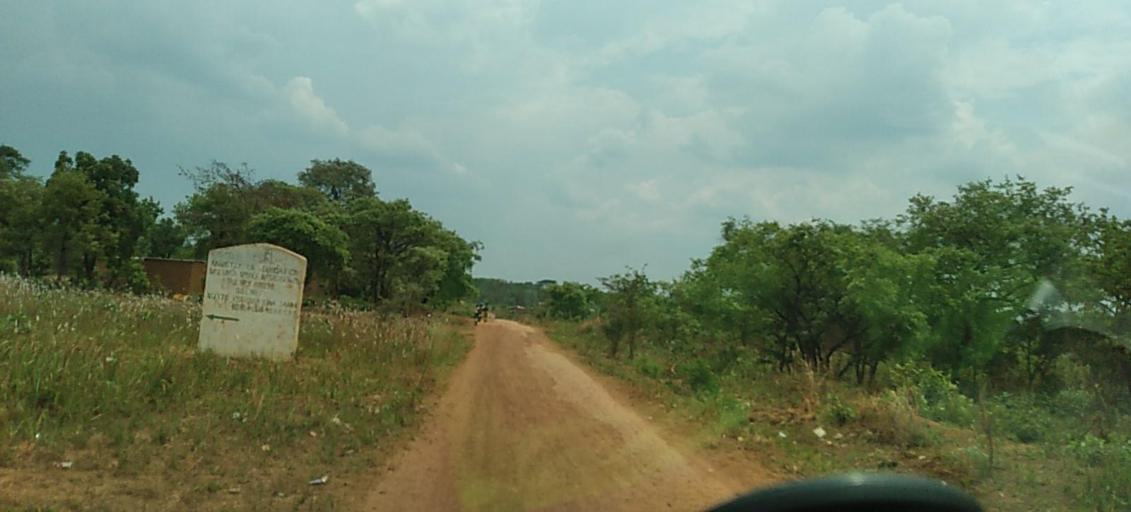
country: ZM
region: North-Western
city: Kansanshi
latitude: -11.9924
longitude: 26.2830
